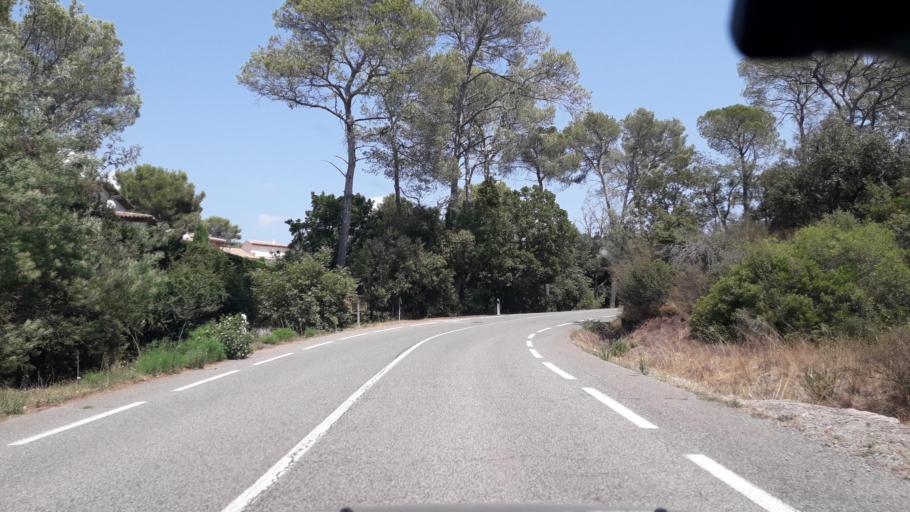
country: FR
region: Provence-Alpes-Cote d'Azur
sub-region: Departement du Var
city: Saint-Raphael
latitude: 43.4435
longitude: 6.8000
